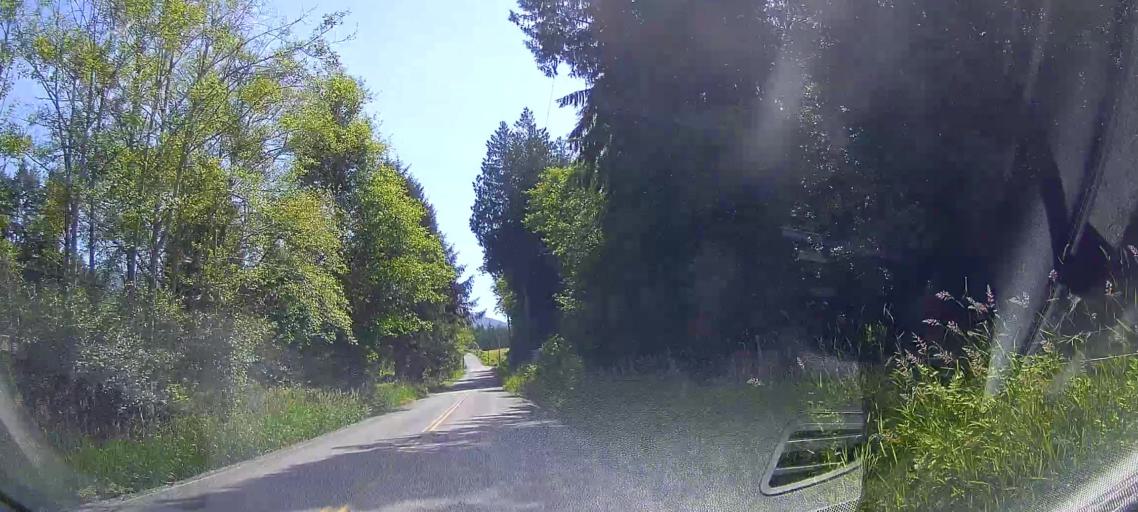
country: US
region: Washington
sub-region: Skagit County
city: Sedro-Woolley
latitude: 48.5577
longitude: -122.2494
